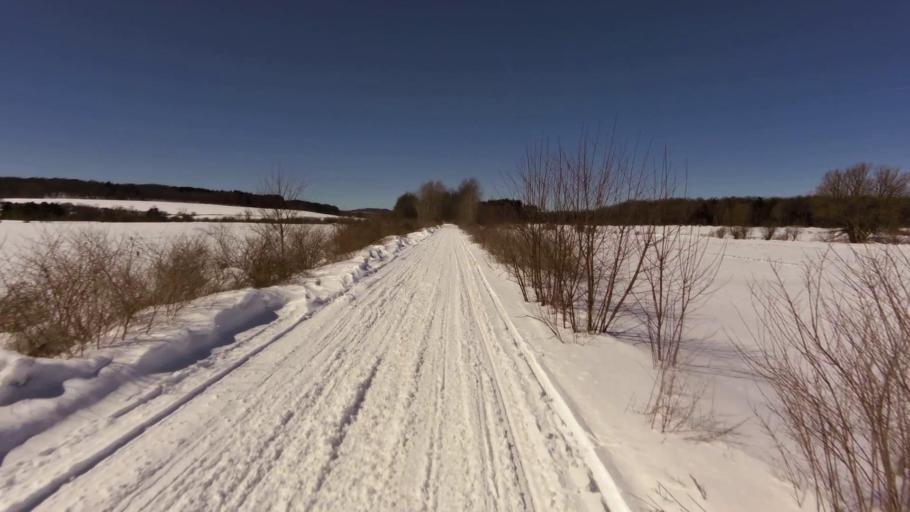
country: US
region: New York
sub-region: Cattaraugus County
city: Delevan
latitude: 42.4305
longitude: -78.3926
